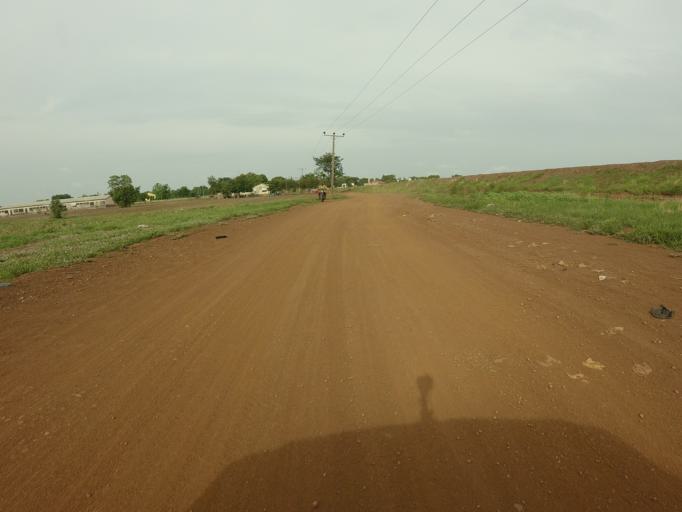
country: GH
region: Northern
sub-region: Yendi
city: Yendi
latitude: 9.9280
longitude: -0.2093
